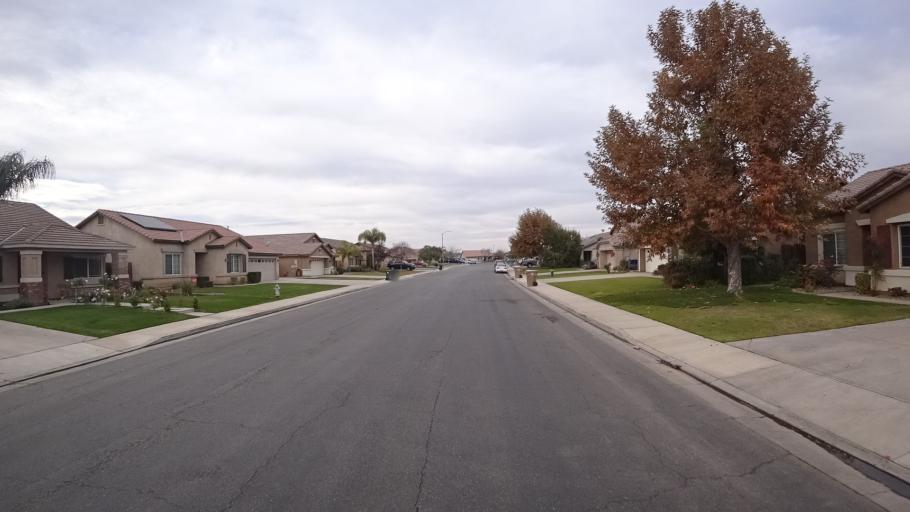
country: US
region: California
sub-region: Kern County
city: Rosedale
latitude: 35.4070
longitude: -119.1510
